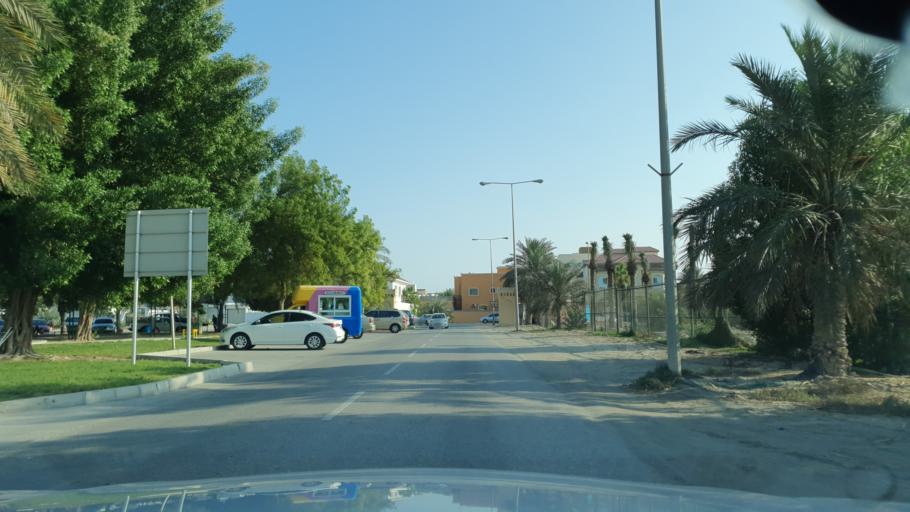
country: BH
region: Manama
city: Jidd Hafs
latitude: 26.2240
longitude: 50.4597
